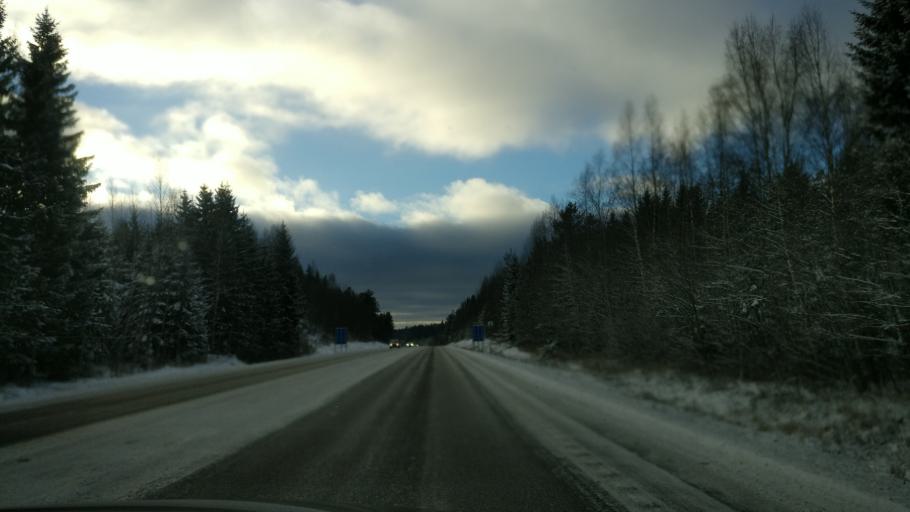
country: FI
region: Paijanne Tavastia
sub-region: Lahti
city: Heinola
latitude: 61.3454
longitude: 26.2022
